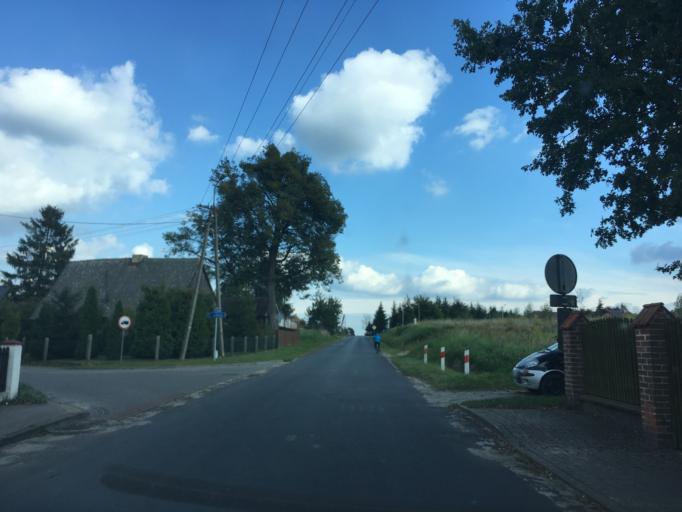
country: PL
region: Kujawsko-Pomorskie
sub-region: Powiat swiecki
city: Osie
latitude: 53.5975
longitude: 18.3522
